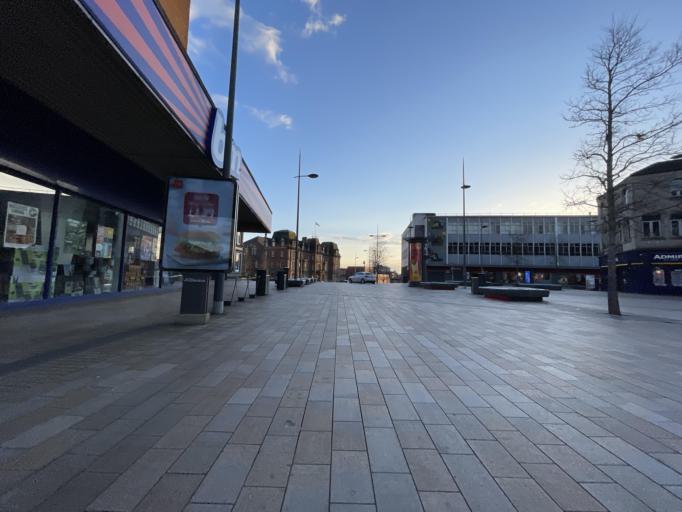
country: GB
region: England
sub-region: Stoke-on-Trent
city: Stoke-on-Trent
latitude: 53.0244
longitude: -2.1743
